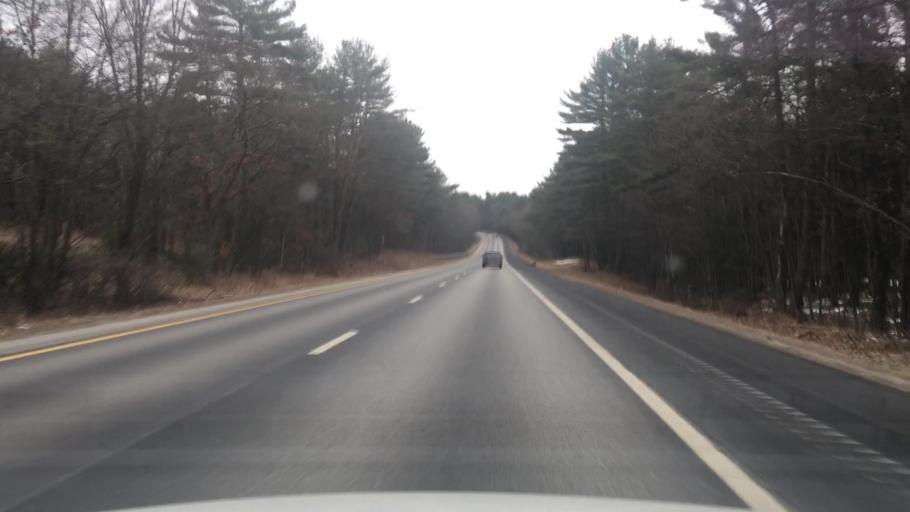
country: US
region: New Hampshire
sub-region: Merrimack County
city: Hopkinton
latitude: 43.1772
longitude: -71.6228
